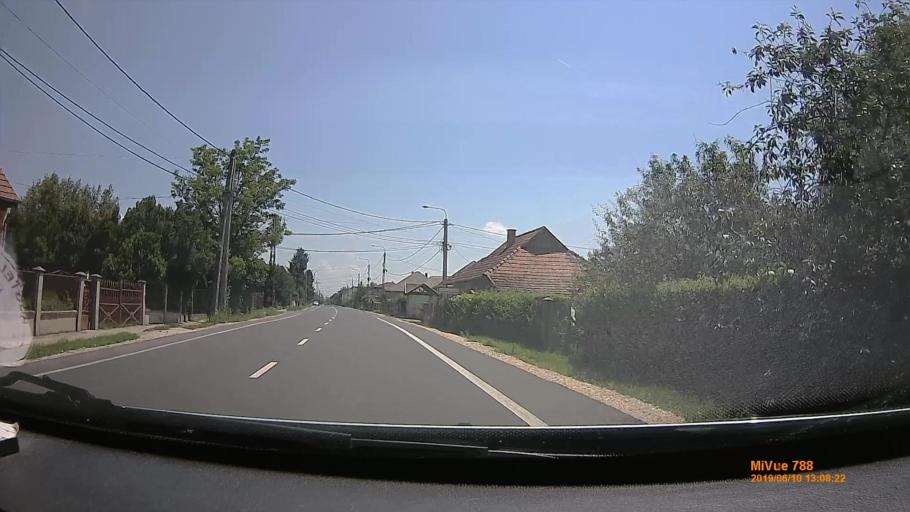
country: HU
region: Borsod-Abauj-Zemplen
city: Hernadnemeti
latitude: 48.0803
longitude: 20.9716
